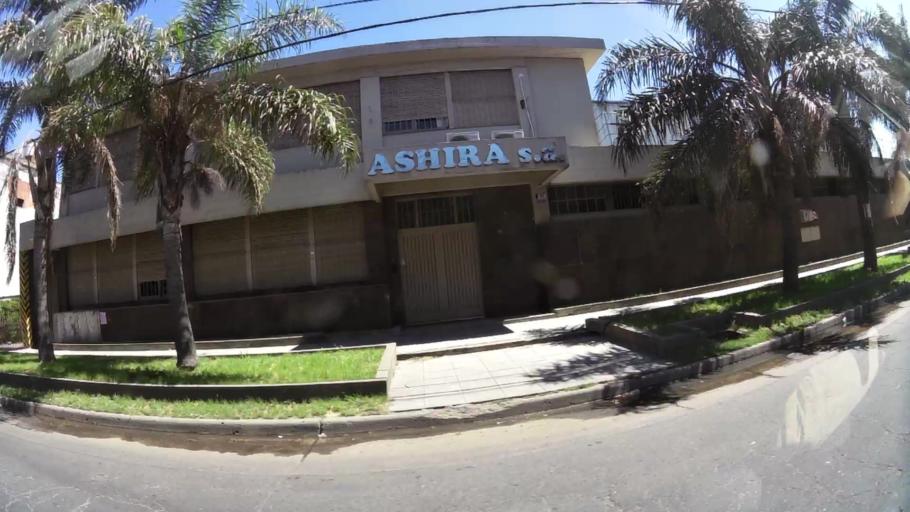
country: AR
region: Buenos Aires
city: Caseros
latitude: -34.5732
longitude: -58.5693
